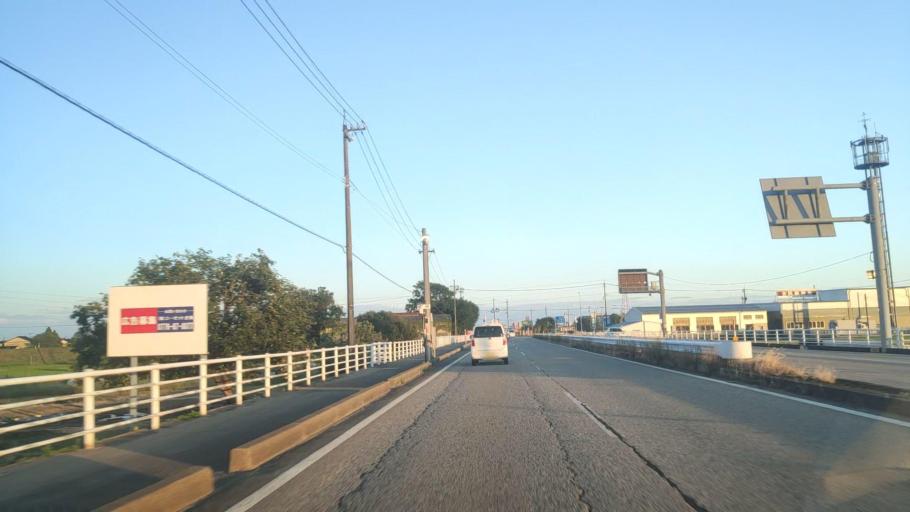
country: JP
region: Toyama
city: Takaoka
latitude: 36.7685
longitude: 137.0031
